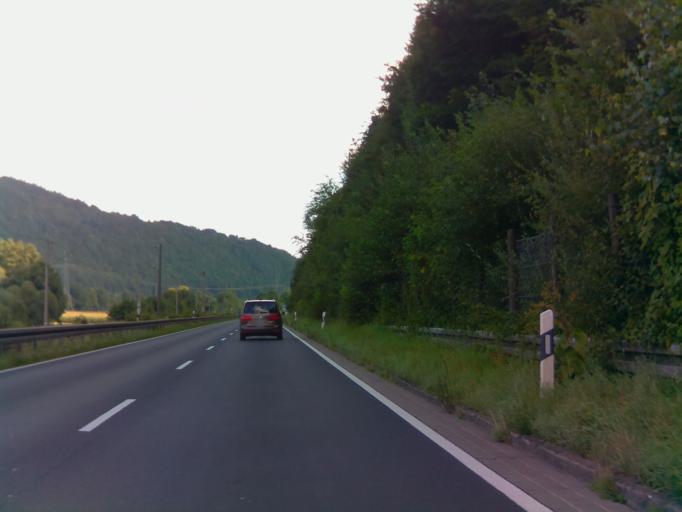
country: DE
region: Bavaria
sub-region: Regierungsbezirk Unterfranken
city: Neuendorf
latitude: 50.0461
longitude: 9.6457
